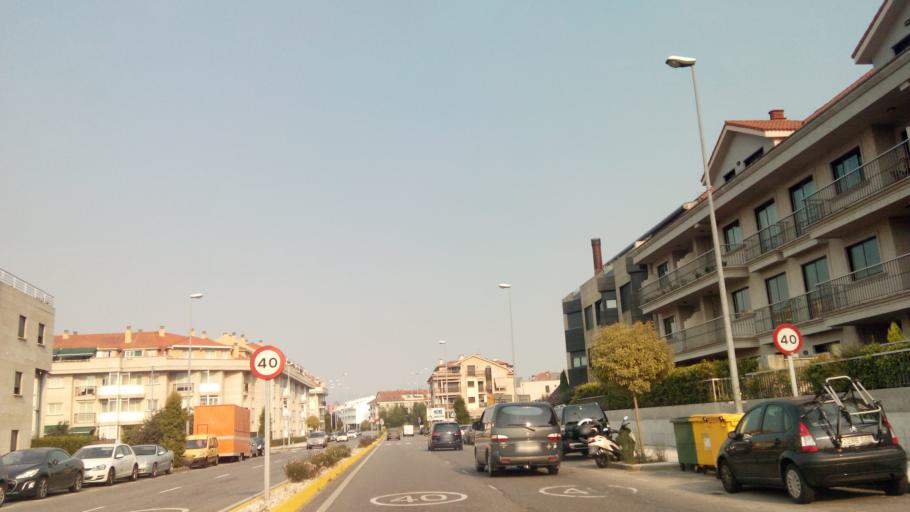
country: ES
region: Galicia
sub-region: Provincia de Pontevedra
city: Baiona
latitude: 42.1104
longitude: -8.8313
